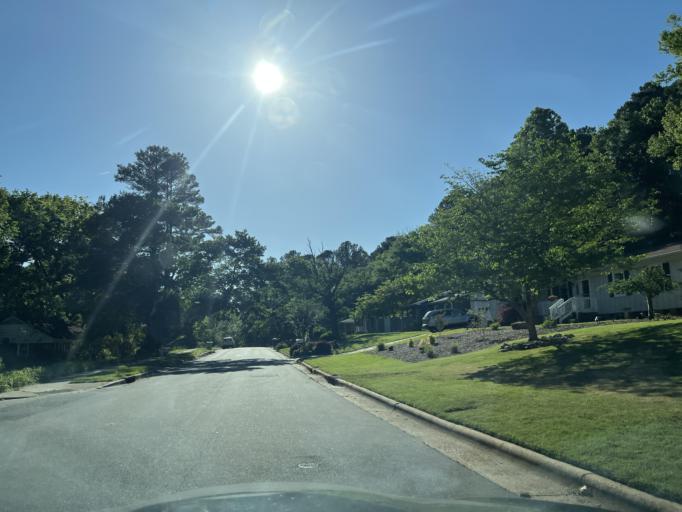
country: US
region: North Carolina
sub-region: Wake County
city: West Raleigh
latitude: 35.8646
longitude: -78.6413
